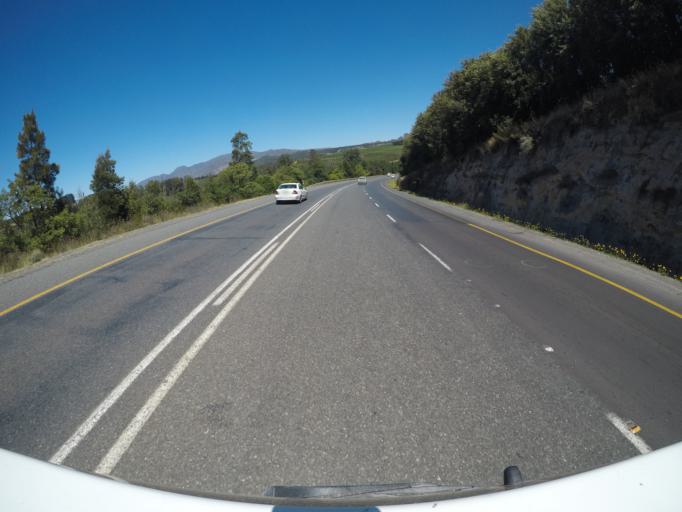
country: ZA
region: Western Cape
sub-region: Overberg District Municipality
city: Grabouw
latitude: -34.1649
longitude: 19.0247
